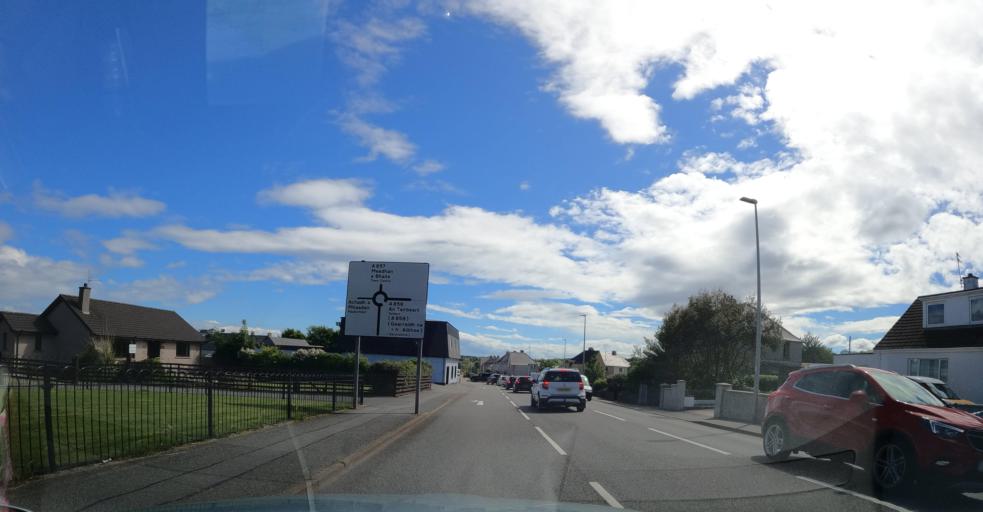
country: GB
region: Scotland
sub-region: Eilean Siar
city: Isle of Lewis
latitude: 58.2201
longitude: -6.3861
